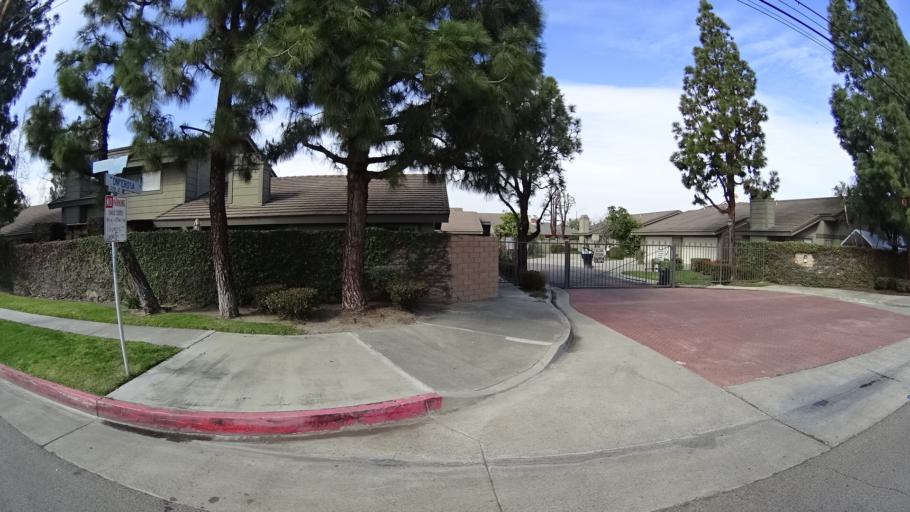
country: US
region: California
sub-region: Orange County
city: Garden Grove
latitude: 33.7925
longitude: -117.9040
